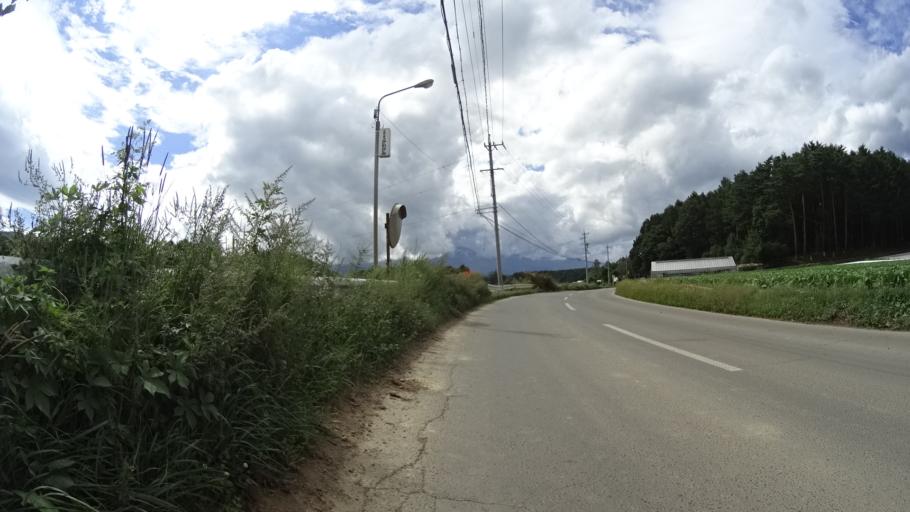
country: JP
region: Nagano
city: Saku
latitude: 35.9644
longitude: 138.5284
